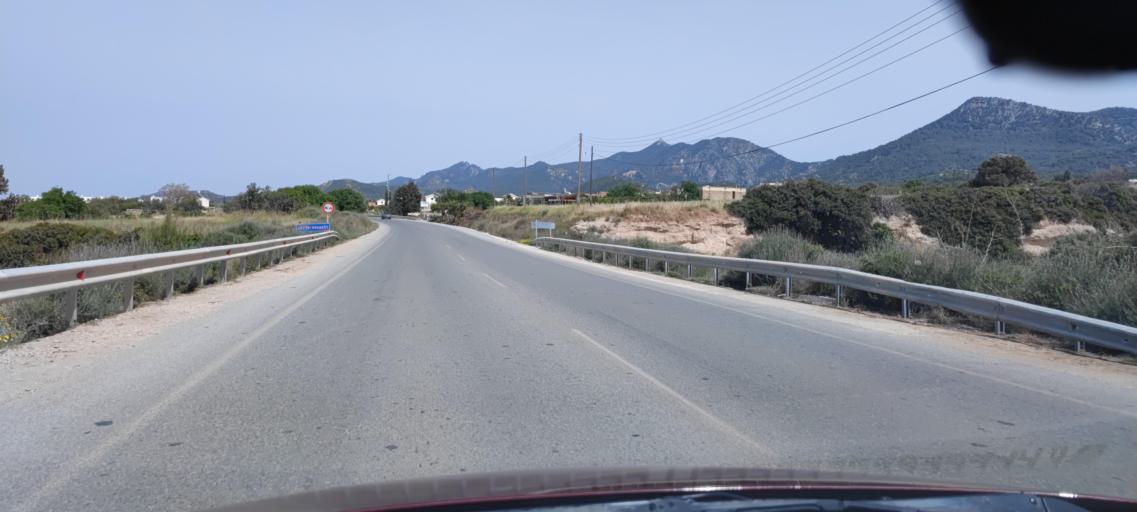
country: CY
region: Ammochostos
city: Lefkonoiko
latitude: 35.3629
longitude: 33.6760
